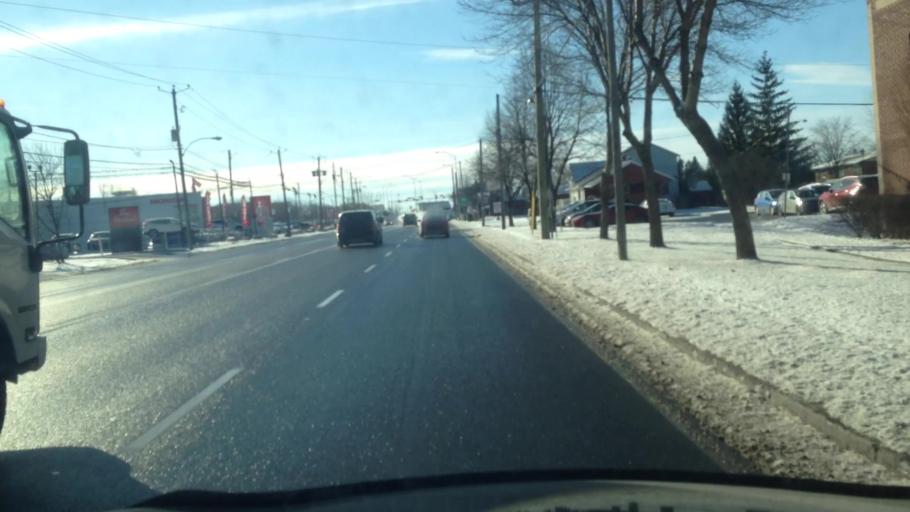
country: CA
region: Quebec
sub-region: Monteregie
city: Mercier
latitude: 45.3466
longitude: -73.7233
